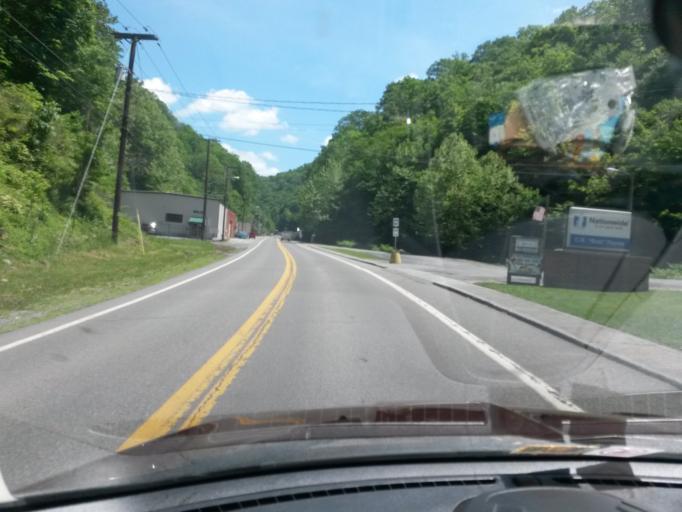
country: US
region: West Virginia
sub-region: McDowell County
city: Welch
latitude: 37.4416
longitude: -81.5714
